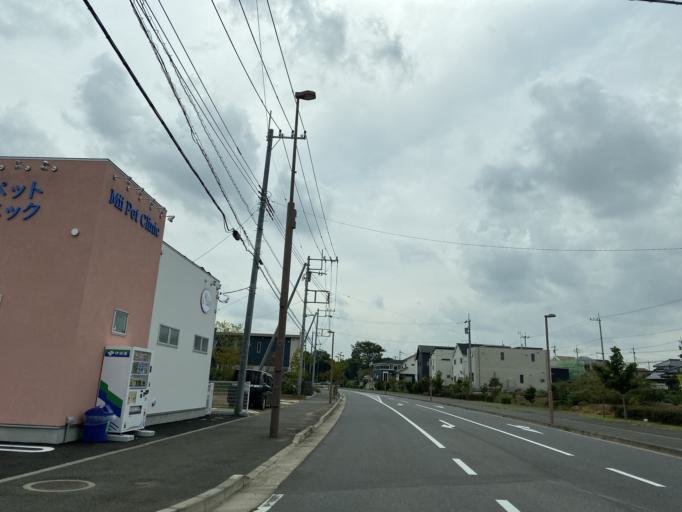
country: JP
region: Ibaraki
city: Mitsukaido
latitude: 36.0178
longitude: 140.0549
